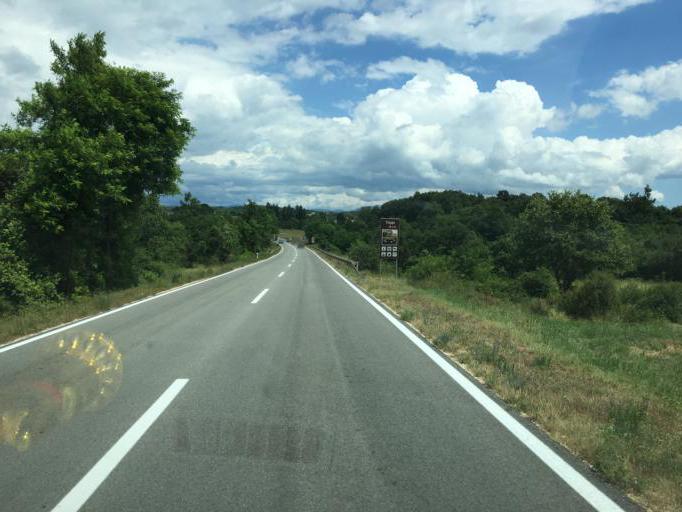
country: HR
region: Istarska
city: Karojba
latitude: 45.2151
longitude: 13.8277
